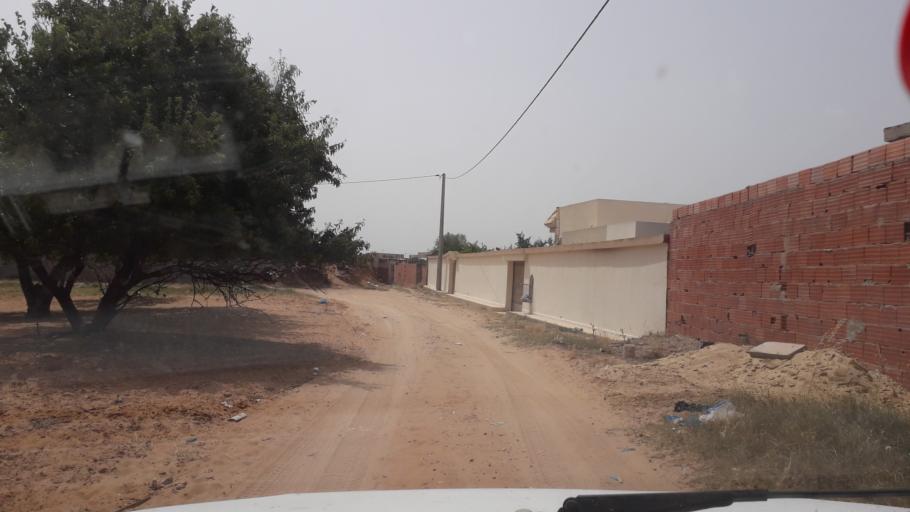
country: TN
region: Safaqis
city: Al Qarmadah
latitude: 34.8099
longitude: 10.7740
